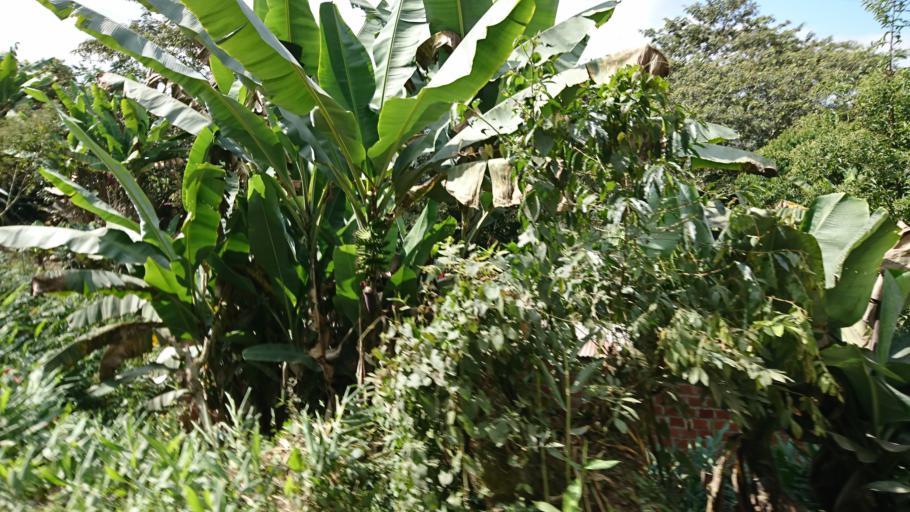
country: BO
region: La Paz
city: Coroico
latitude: -16.1176
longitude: -67.7660
